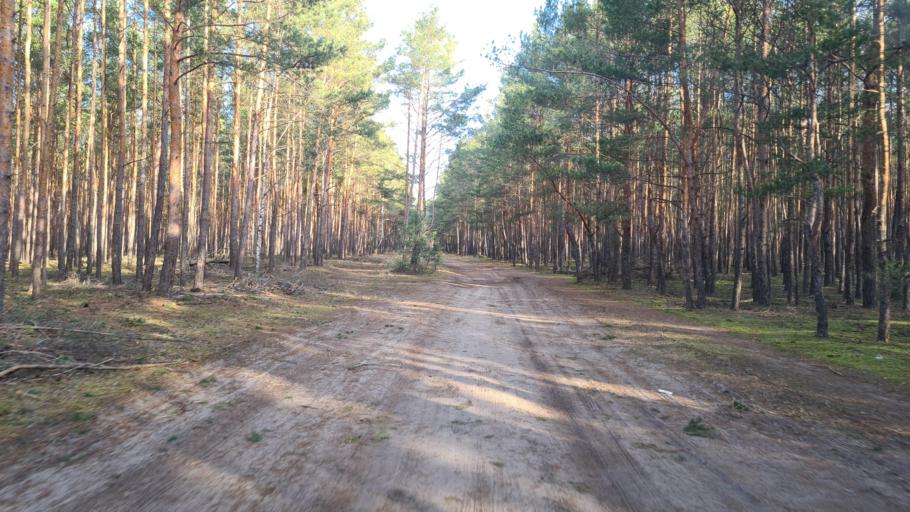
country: DE
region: Brandenburg
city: Gross Koris
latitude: 52.1537
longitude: 13.6921
